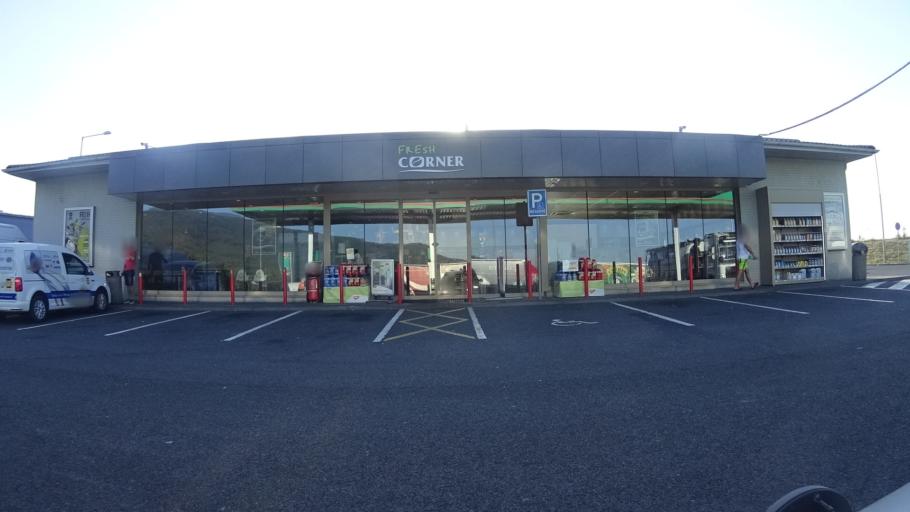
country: CZ
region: Ustecky
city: Chlumec
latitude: 50.7121
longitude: 13.9697
